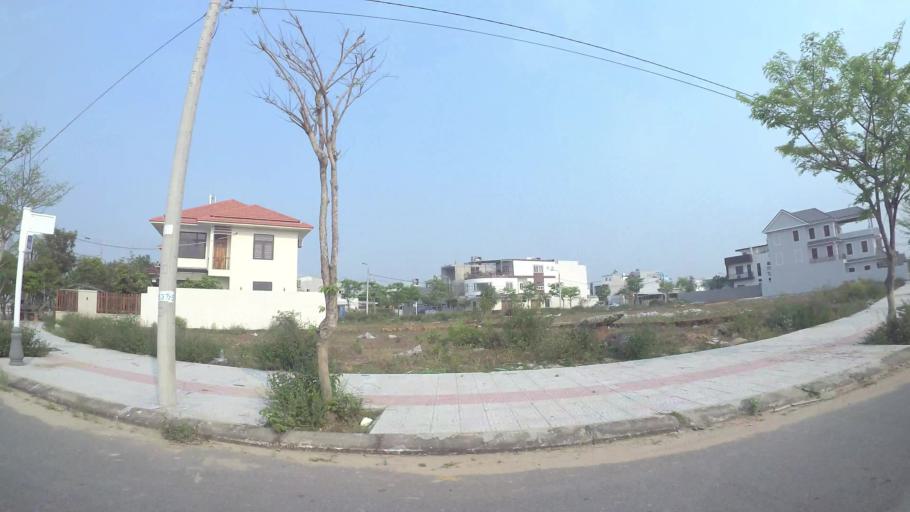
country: VN
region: Da Nang
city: Cam Le
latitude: 16.0035
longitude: 108.2280
